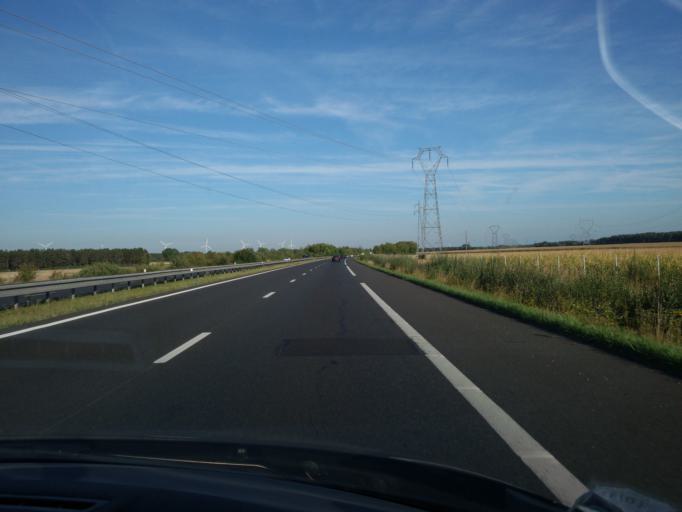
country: FR
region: Centre
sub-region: Departement du Cher
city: Marmagne
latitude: 47.0679
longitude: 2.2877
